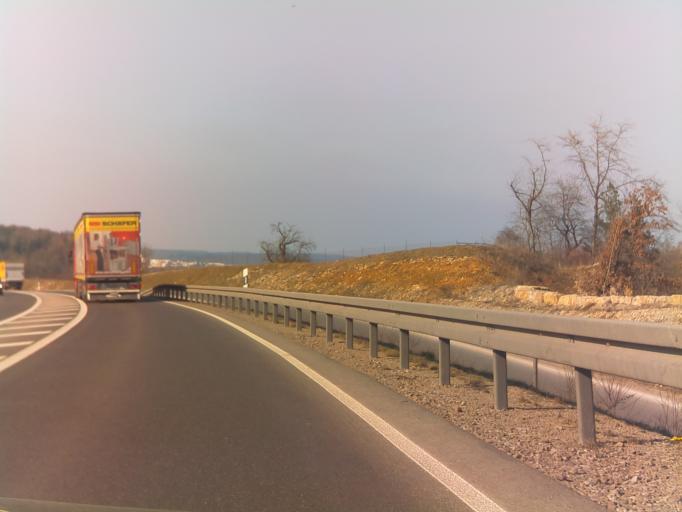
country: DE
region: Baden-Wuerttemberg
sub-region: Regierungsbezirk Stuttgart
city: Magstadt
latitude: 48.7461
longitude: 8.9489
